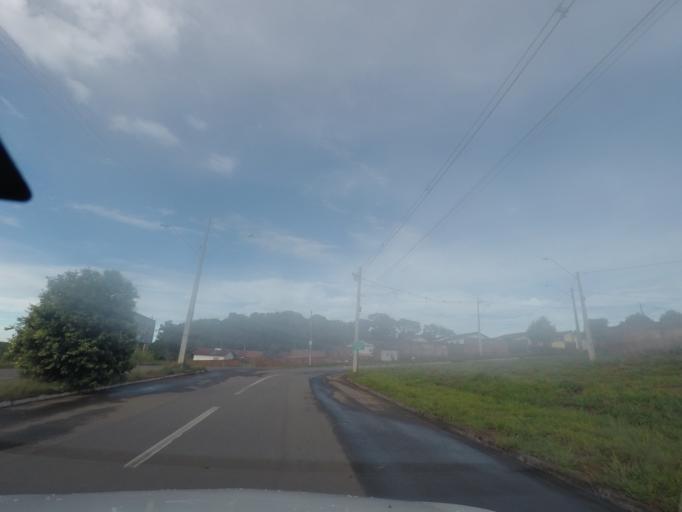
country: BR
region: Goias
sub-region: Aparecida De Goiania
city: Aparecida de Goiania
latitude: -16.7852
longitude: -49.3799
